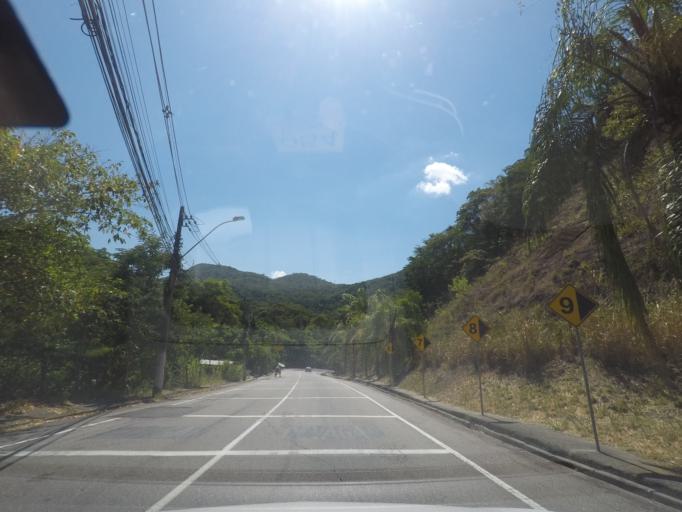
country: BR
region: Rio de Janeiro
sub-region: Niteroi
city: Niteroi
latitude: -22.9256
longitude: -43.0645
